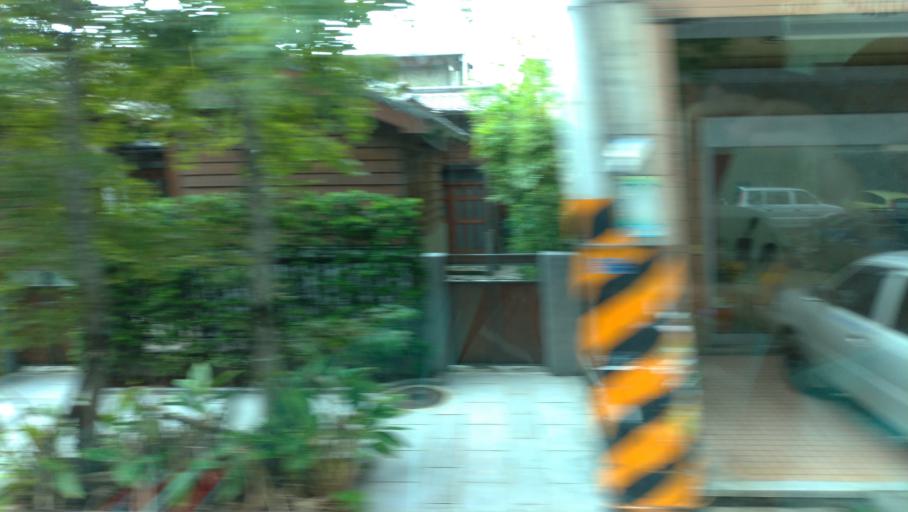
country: TW
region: Taiwan
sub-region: Keelung
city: Keelung
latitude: 25.1448
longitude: 121.7616
